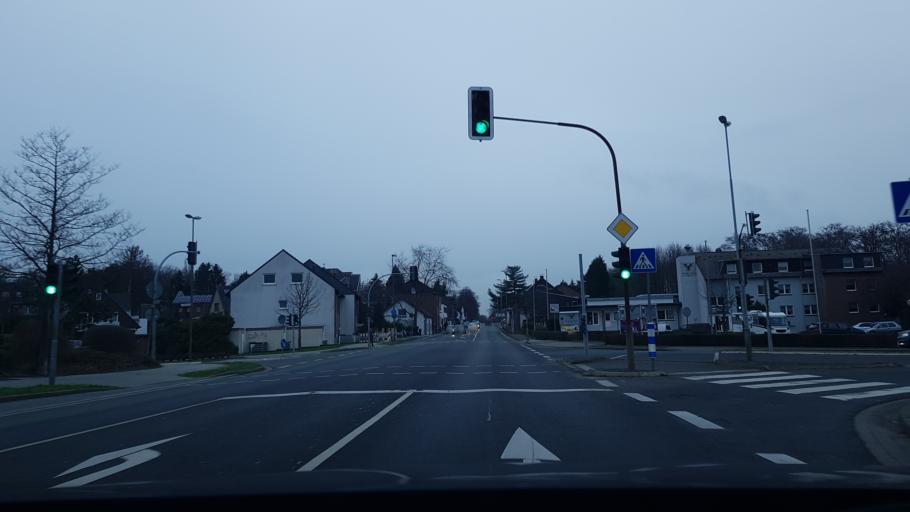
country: DE
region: North Rhine-Westphalia
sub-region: Regierungsbezirk Dusseldorf
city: Moers
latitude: 51.4205
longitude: 6.6553
